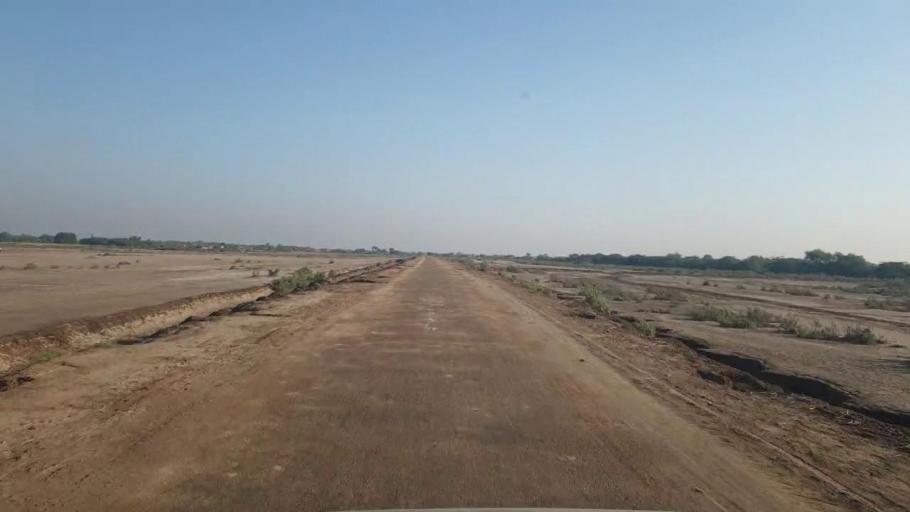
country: PK
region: Sindh
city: Badin
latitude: 24.7192
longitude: 68.8611
